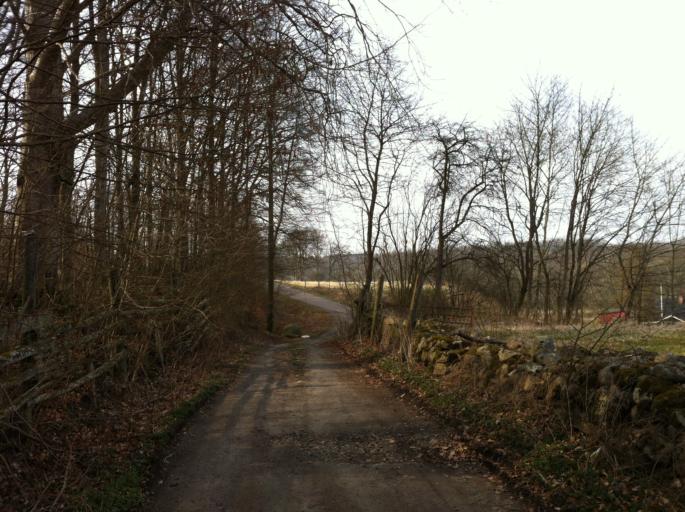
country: SE
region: Skane
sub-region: Eslovs Kommun
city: Stehag
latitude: 56.0164
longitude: 13.3844
